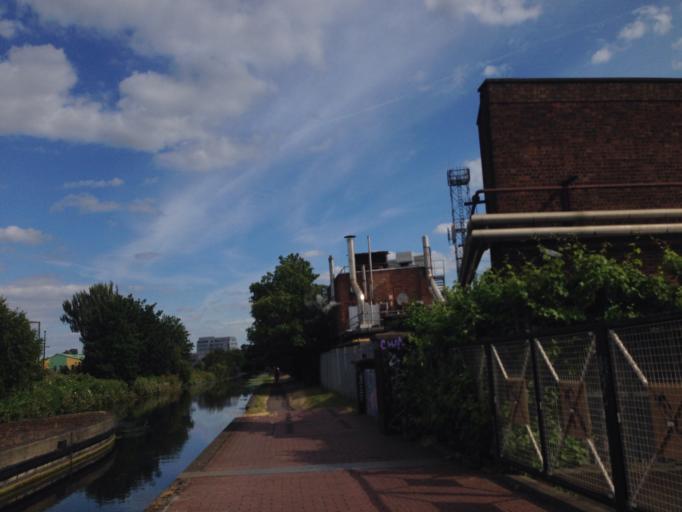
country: GB
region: England
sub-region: Greater London
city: Wembley
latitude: 51.5380
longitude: -0.2818
